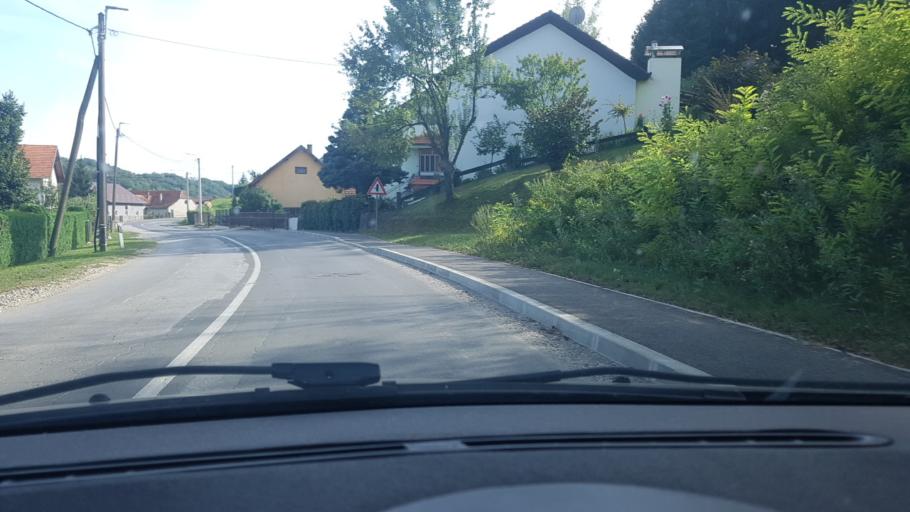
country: HR
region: Krapinsko-Zagorska
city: Zlatar
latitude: 46.0968
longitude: 16.0789
